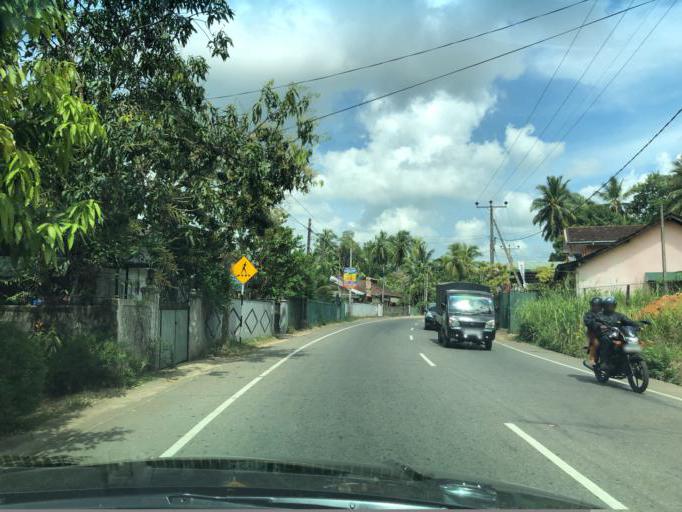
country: LK
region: Western
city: Horawala Junction
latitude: 6.5233
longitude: 80.1084
